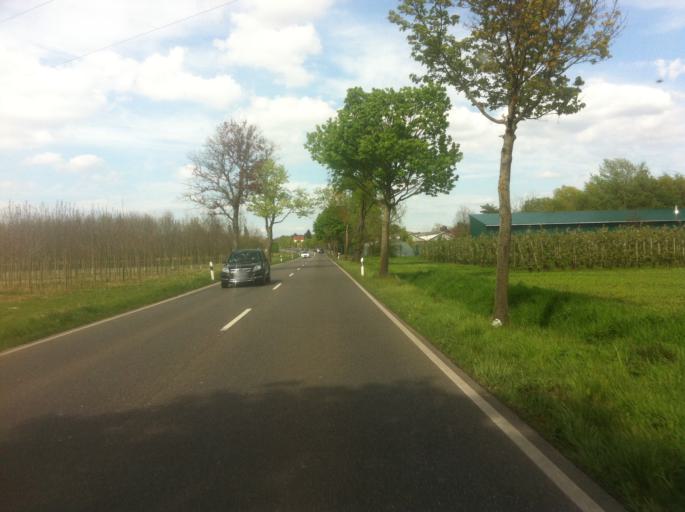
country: DE
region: North Rhine-Westphalia
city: Meckenheim
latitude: 50.6362
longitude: 7.0321
